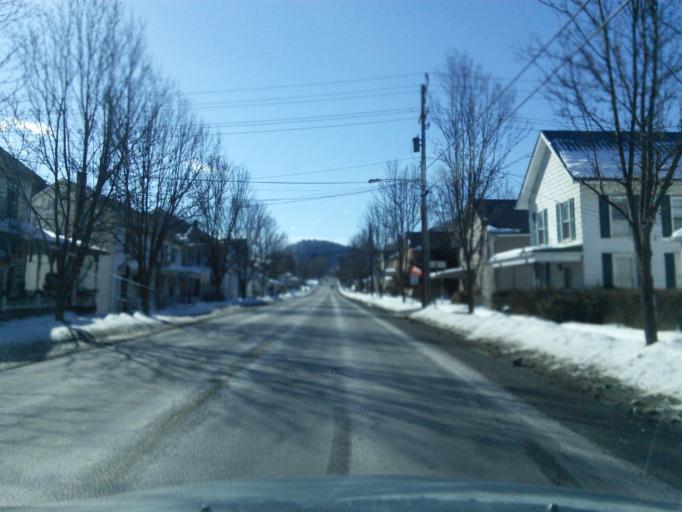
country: US
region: Pennsylvania
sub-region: Centre County
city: Milesburg
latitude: 40.9404
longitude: -77.7854
